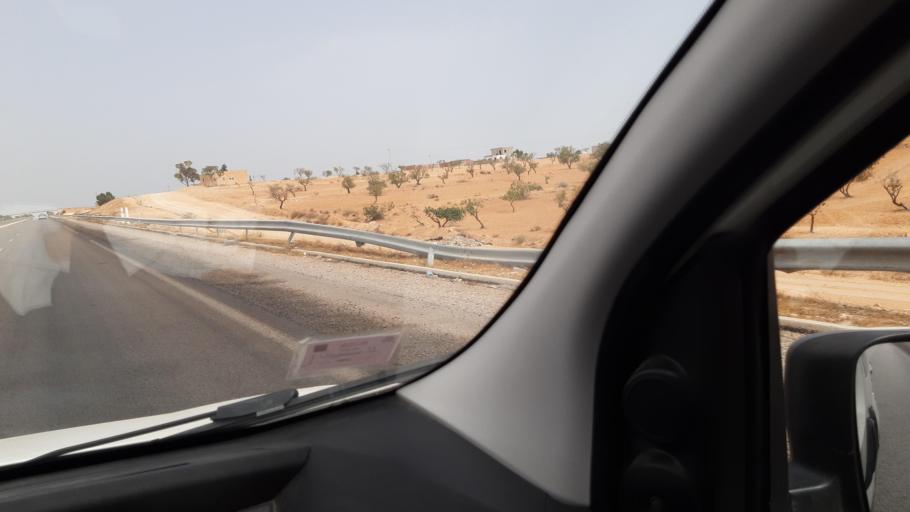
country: TN
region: Safaqis
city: Sfax
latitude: 34.8389
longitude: 10.6634
